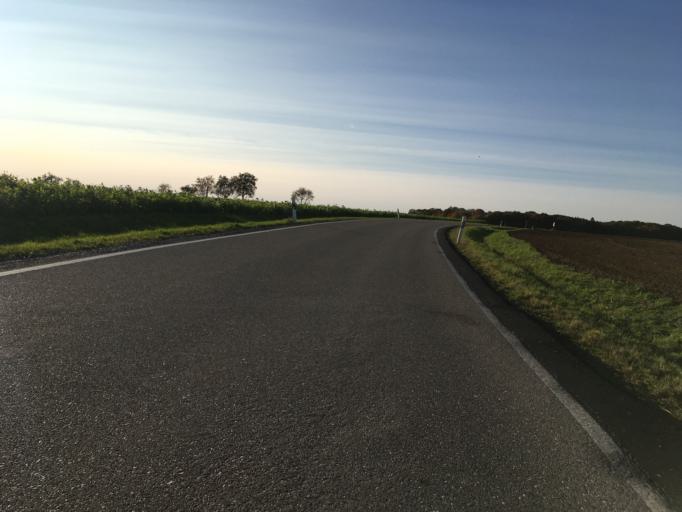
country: DE
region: Baden-Wuerttemberg
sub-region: Regierungsbezirk Stuttgart
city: Kupferzell
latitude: 49.2315
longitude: 9.6649
